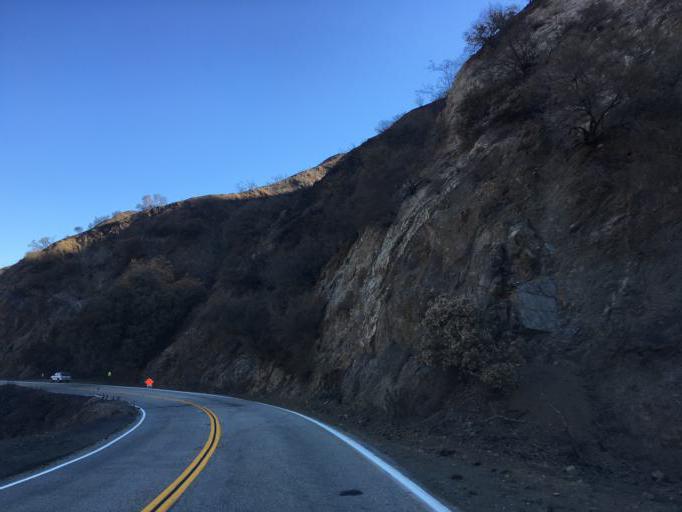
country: US
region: California
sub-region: Los Angeles County
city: San Fernando
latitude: 34.3719
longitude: -118.3987
